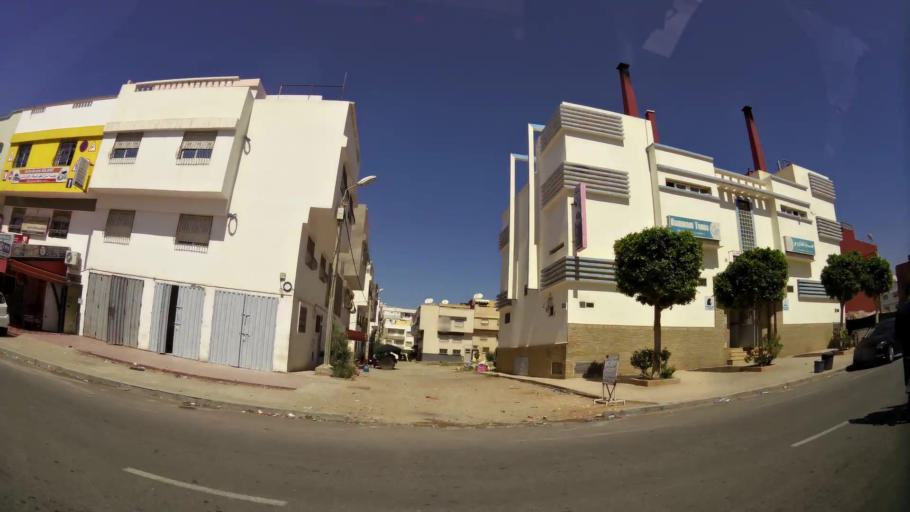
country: MA
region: Oued ed Dahab-Lagouira
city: Dakhla
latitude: 30.4301
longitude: -9.5614
